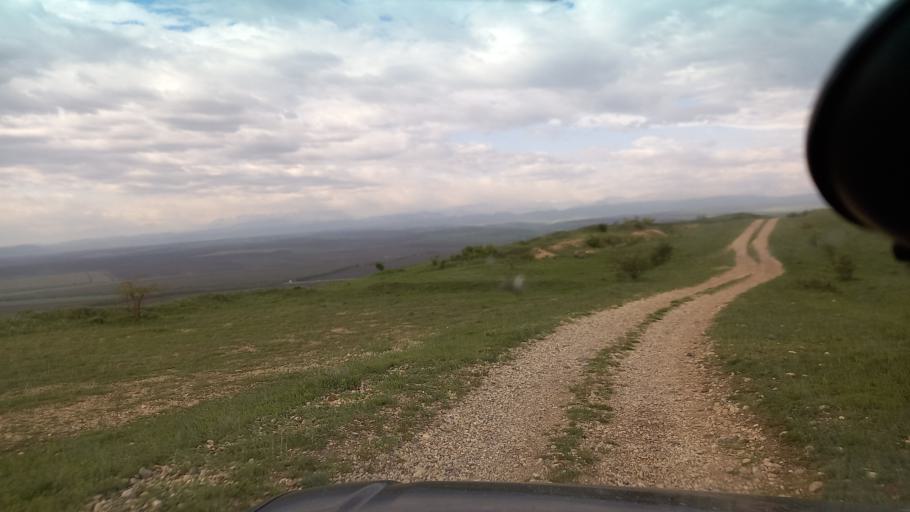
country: RU
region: Kabardino-Balkariya
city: Kuba-Taba
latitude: 43.8063
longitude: 43.4080
